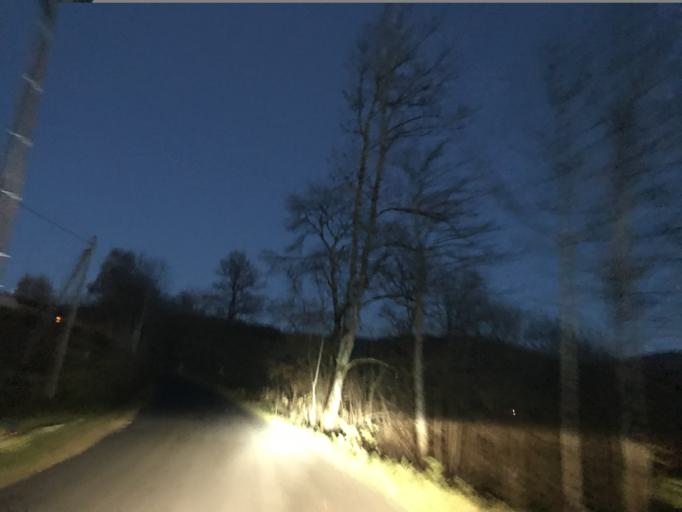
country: FR
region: Rhone-Alpes
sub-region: Departement de la Loire
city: Noiretable
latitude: 45.7309
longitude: 3.7284
